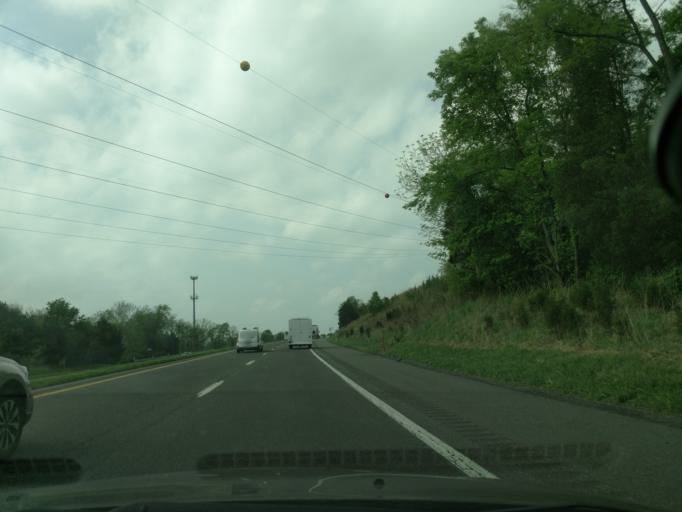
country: US
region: Pennsylvania
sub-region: Berks County
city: Flying Hills
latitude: 40.2644
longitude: -75.9156
